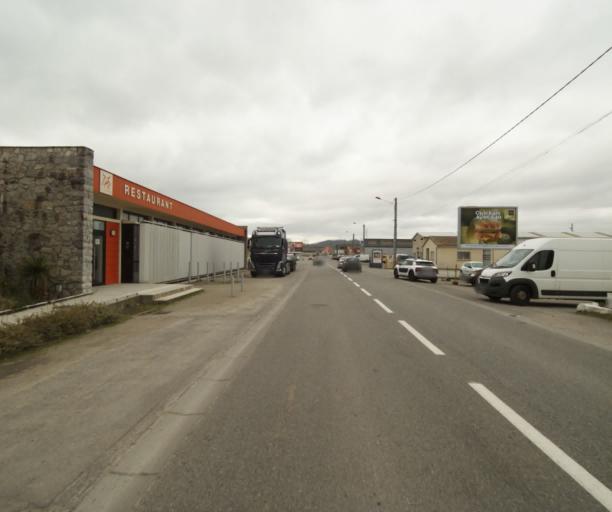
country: FR
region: Midi-Pyrenees
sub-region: Departement de l'Ariege
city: Pamiers
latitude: 43.1281
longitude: 1.6217
